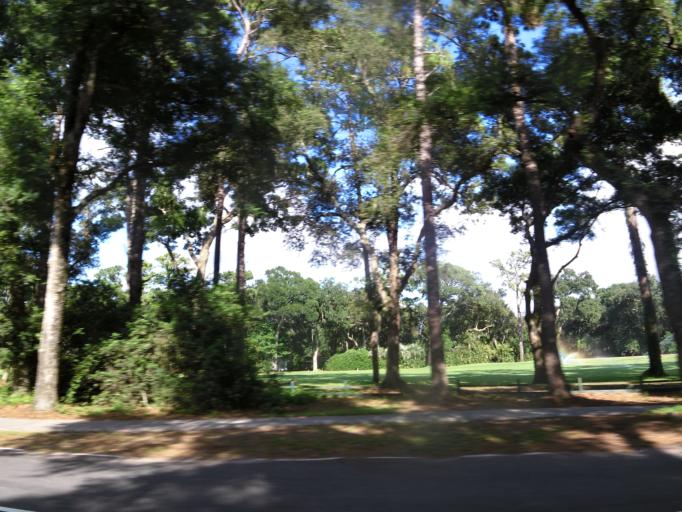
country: US
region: Georgia
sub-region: Glynn County
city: Saint Simon Mills
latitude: 31.1967
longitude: -81.3762
